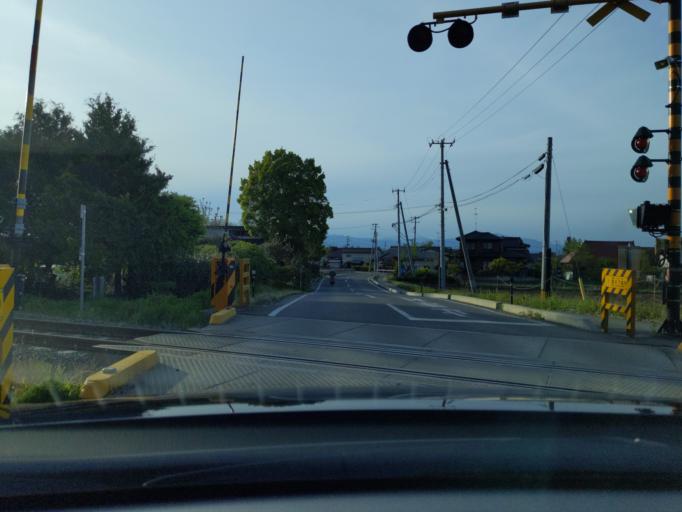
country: JP
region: Fukushima
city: Koriyama
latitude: 37.3420
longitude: 140.3791
